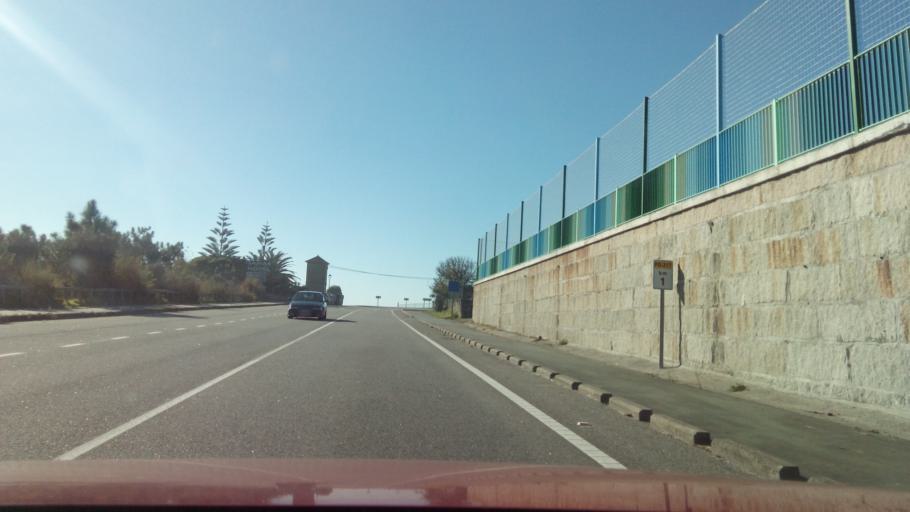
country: ES
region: Galicia
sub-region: Provincia de Pontevedra
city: O Grove
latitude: 42.4586
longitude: -8.8831
